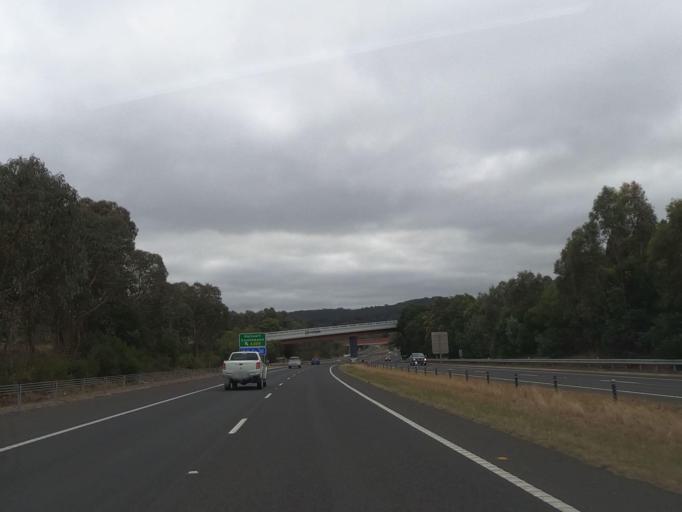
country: AU
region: Victoria
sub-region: Mount Alexander
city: Castlemaine
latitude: -37.0108
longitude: 144.2521
